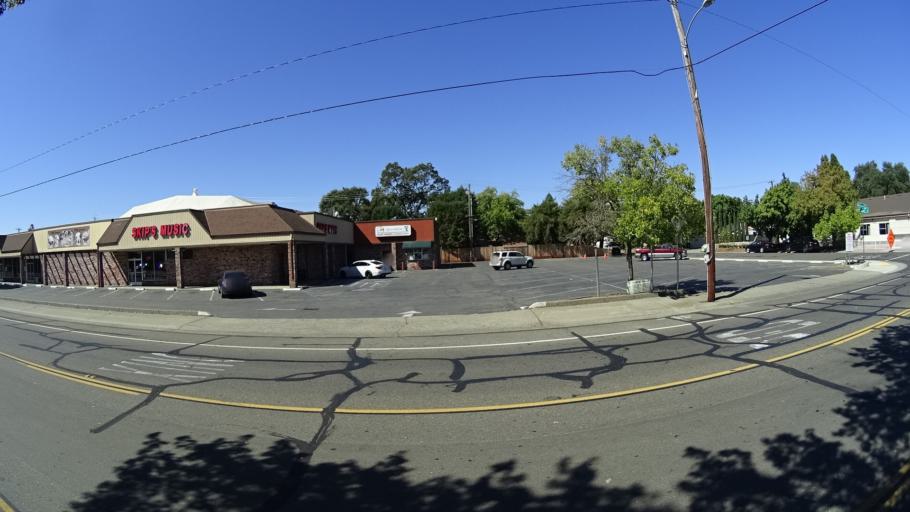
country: US
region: California
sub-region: Sacramento County
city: Elk Grove
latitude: 38.4071
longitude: -121.3715
